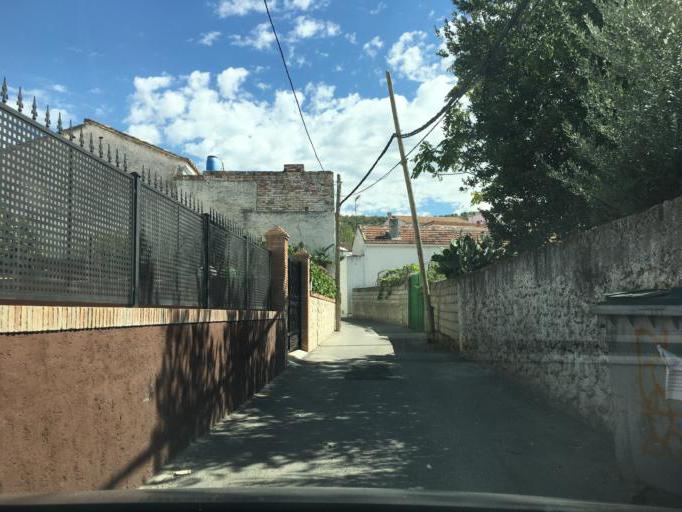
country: ES
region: Andalusia
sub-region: Provincia de Granada
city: Beas de Granada
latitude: 37.2176
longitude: -3.4805
